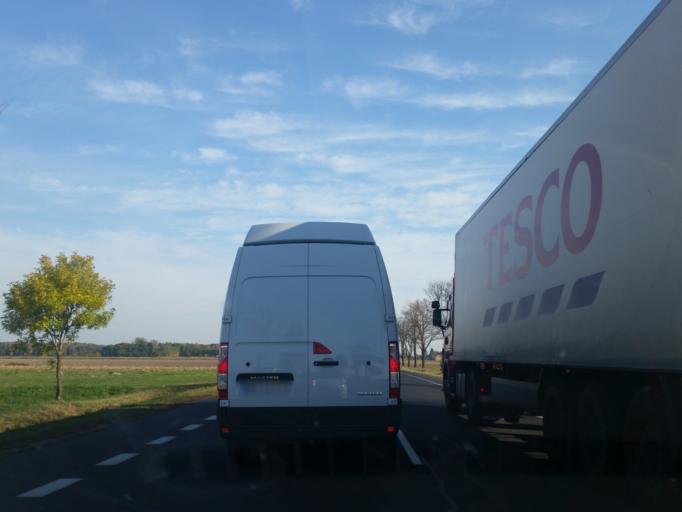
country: PL
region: Masovian Voivodeship
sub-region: Powiat sierpecki
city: Zawidz
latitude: 52.8033
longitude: 19.8489
